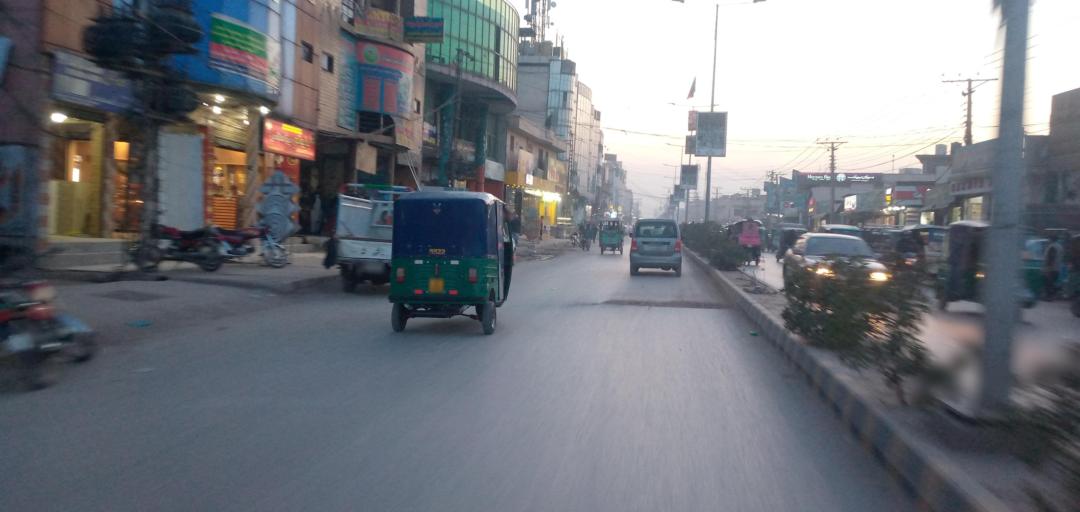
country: PK
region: Khyber Pakhtunkhwa
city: Peshawar
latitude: 34.0281
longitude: 71.6000
